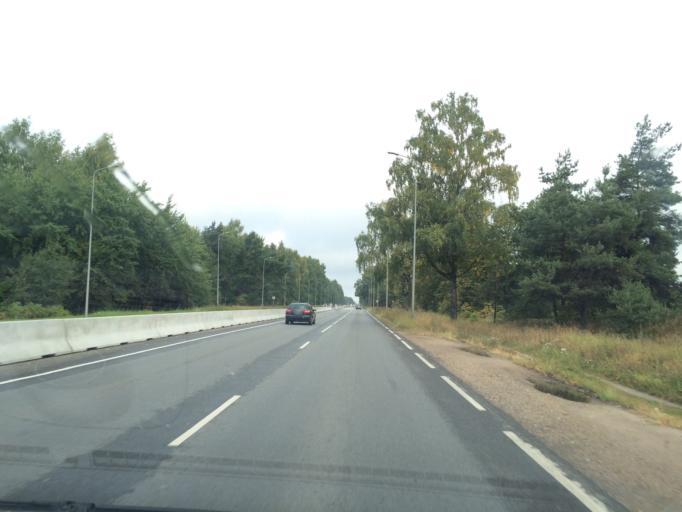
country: LV
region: Kekava
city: Kekava
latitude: 56.8710
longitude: 24.2725
